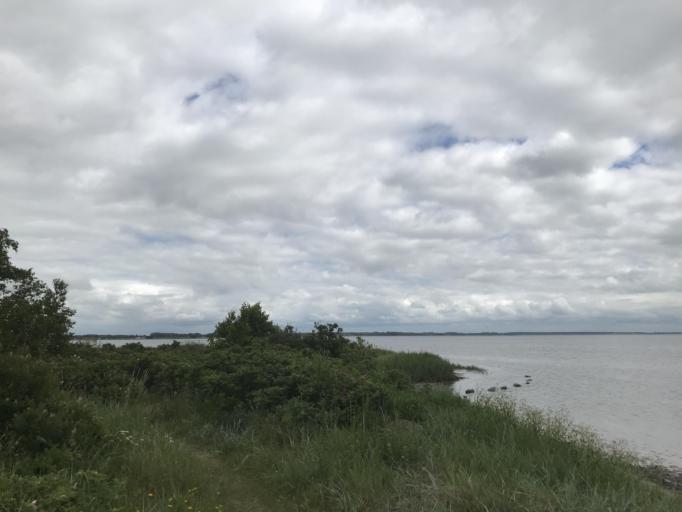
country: SE
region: Skane
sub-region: Landskrona
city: Landskrona
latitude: 55.8567
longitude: 12.8541
